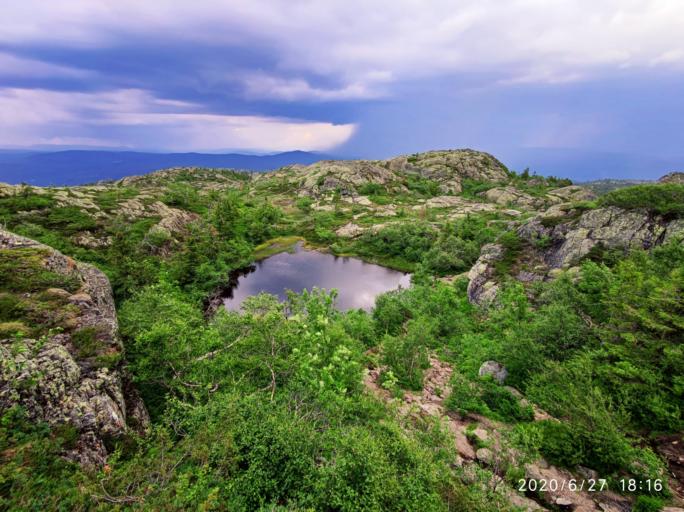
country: NO
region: Buskerud
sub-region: Kongsberg
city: Kongsberg
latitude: 59.6724
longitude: 9.5222
